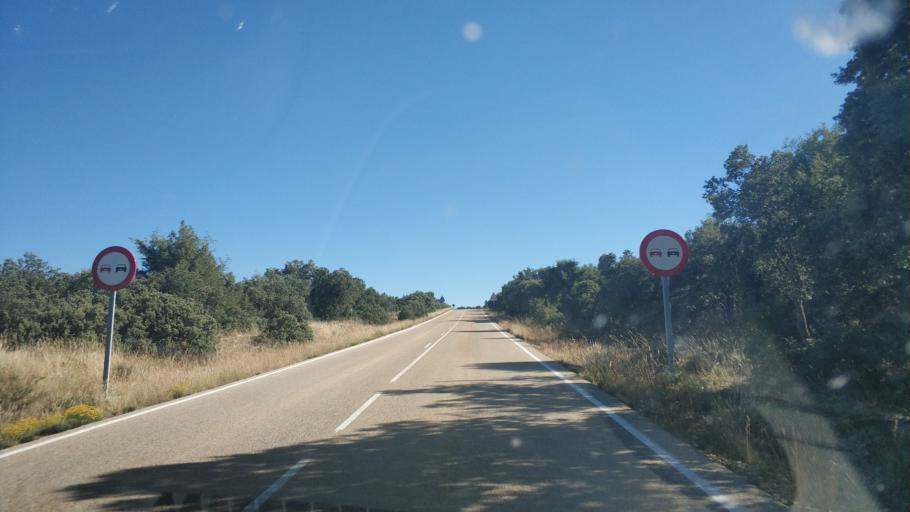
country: ES
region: Castille and Leon
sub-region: Provincia de Soria
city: Montejo de Tiermes
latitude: 41.4079
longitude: -3.2018
